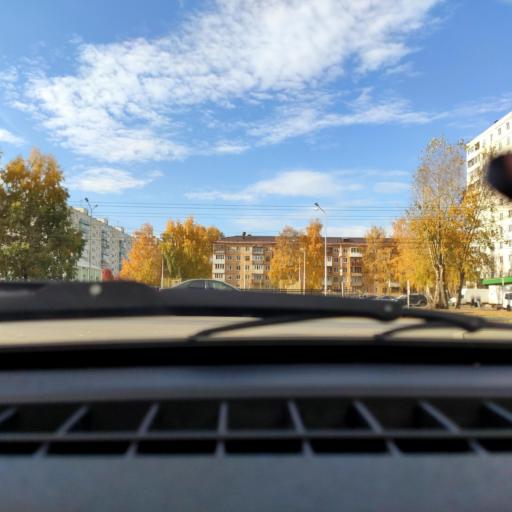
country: RU
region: Bashkortostan
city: Ufa
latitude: 54.8092
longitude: 56.1308
